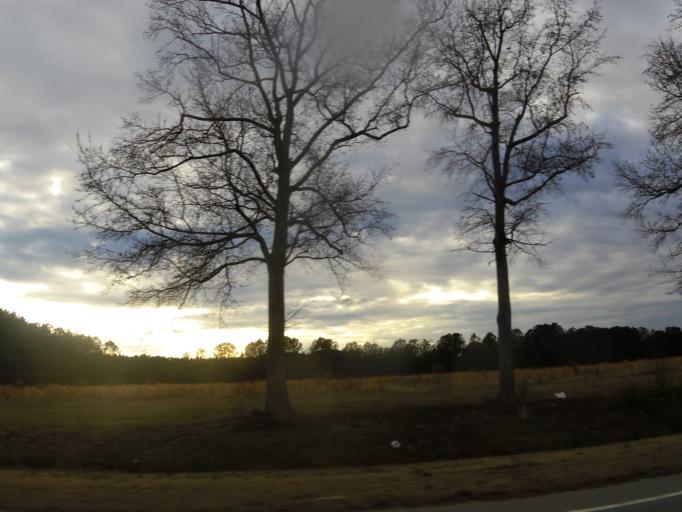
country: US
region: North Carolina
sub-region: Nash County
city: Sharpsburg
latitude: 35.8976
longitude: -77.8251
